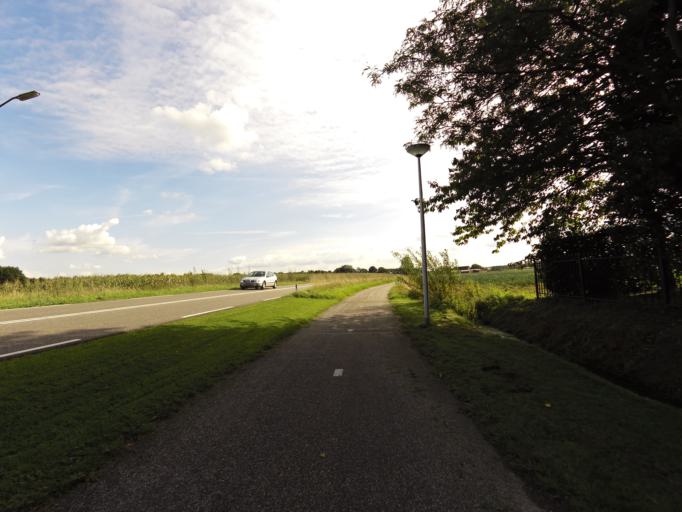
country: NL
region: North Brabant
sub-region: Gemeente Woensdrecht
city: Woensdrecht
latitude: 51.4547
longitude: 4.3778
